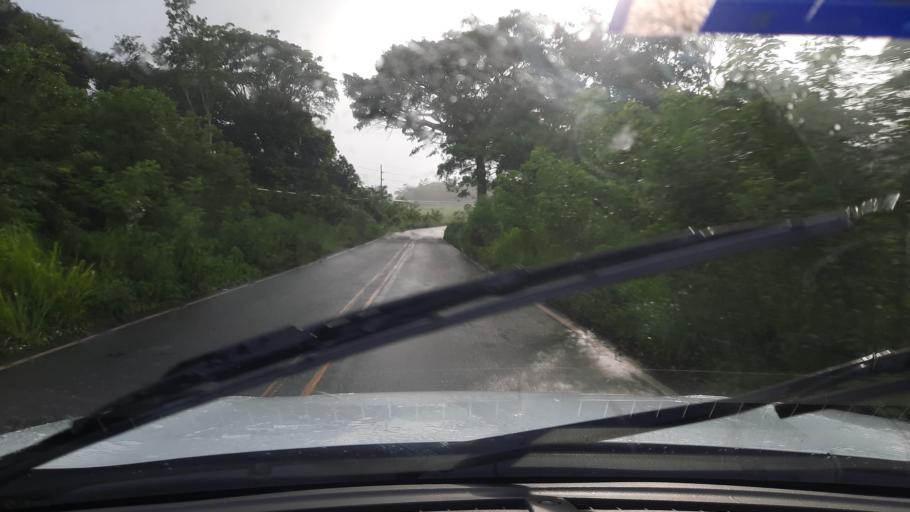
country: CR
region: Guanacaste
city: La Cruz
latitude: 11.0452
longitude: -85.4853
